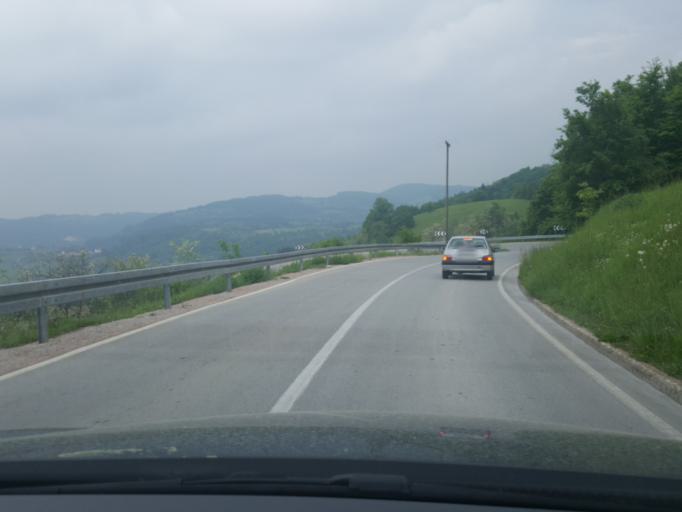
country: RS
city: Kamenica
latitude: 44.2043
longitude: 19.7213
